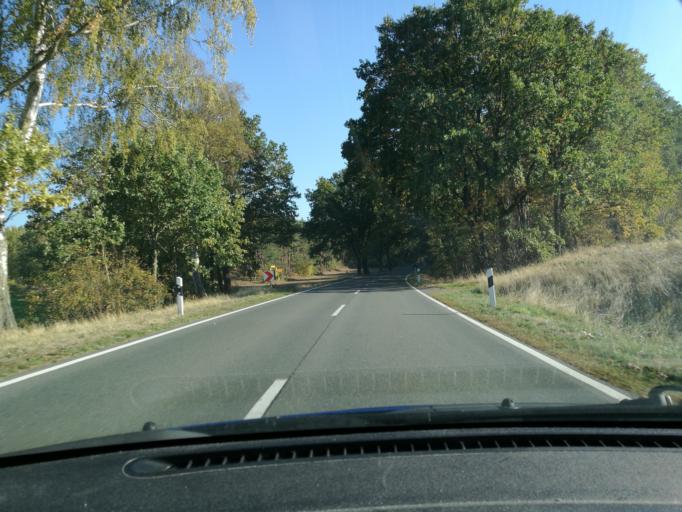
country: DE
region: Lower Saxony
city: Karwitz
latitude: 53.1272
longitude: 10.9745
